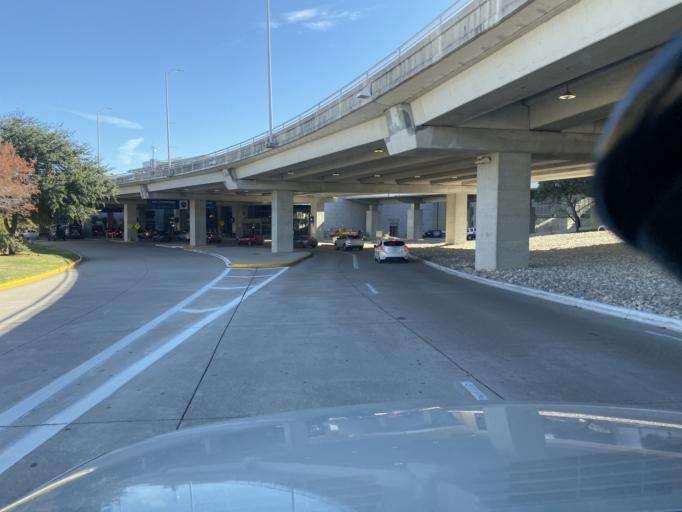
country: US
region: Texas
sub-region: Travis County
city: Hornsby Bend
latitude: 30.2030
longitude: -97.6690
